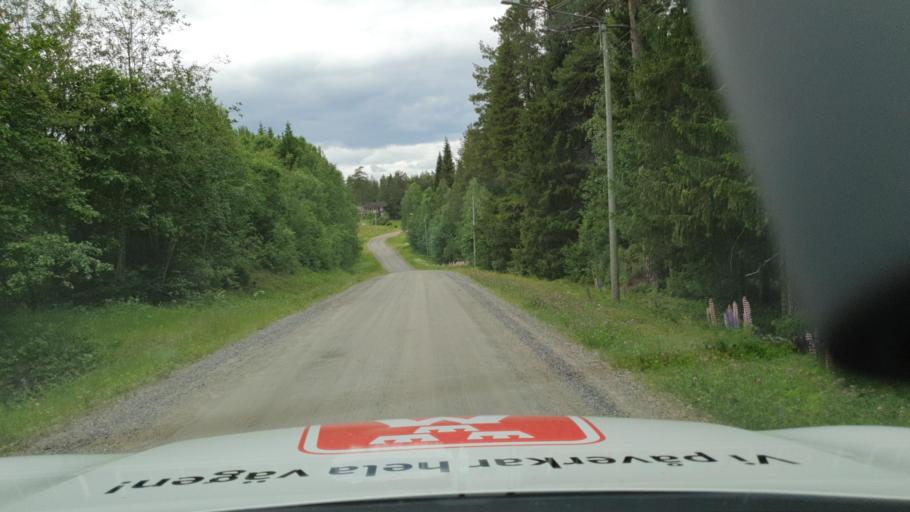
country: SE
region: Vaesterbotten
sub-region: Bjurholms Kommun
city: Bjurholm
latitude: 63.7415
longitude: 19.2824
